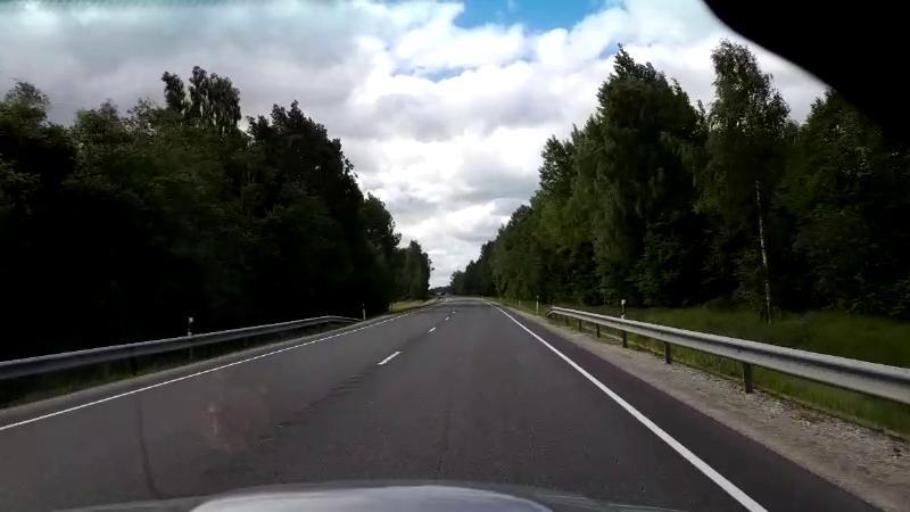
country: EE
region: Raplamaa
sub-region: Maerjamaa vald
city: Marjamaa
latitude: 58.8167
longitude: 24.4125
